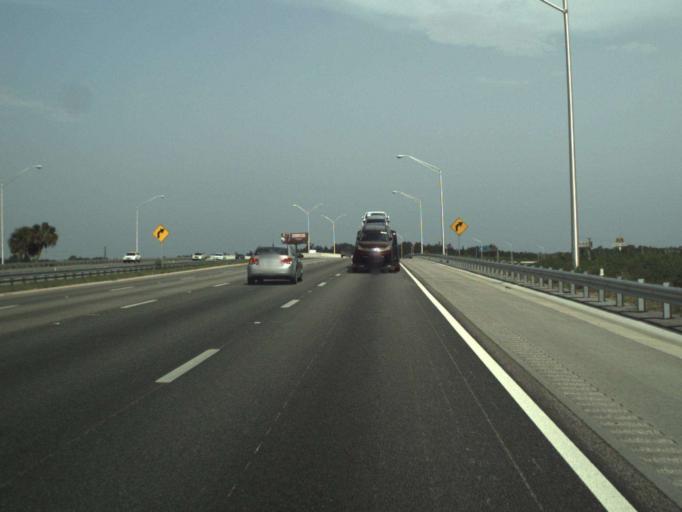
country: US
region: Florida
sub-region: Saint Lucie County
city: Lakewood Park
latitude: 27.4561
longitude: -80.4016
